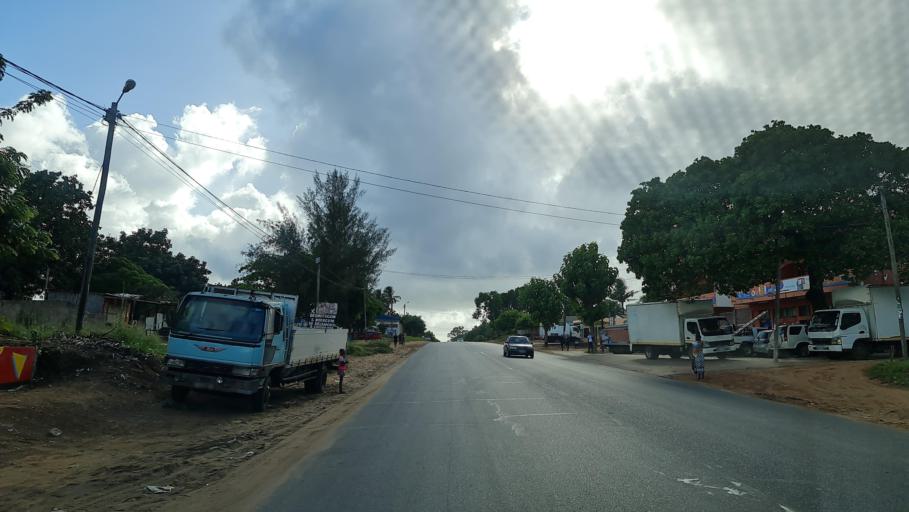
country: MZ
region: Gaza
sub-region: Xai-Xai District
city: Xai-Xai
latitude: -25.0570
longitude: 33.6818
